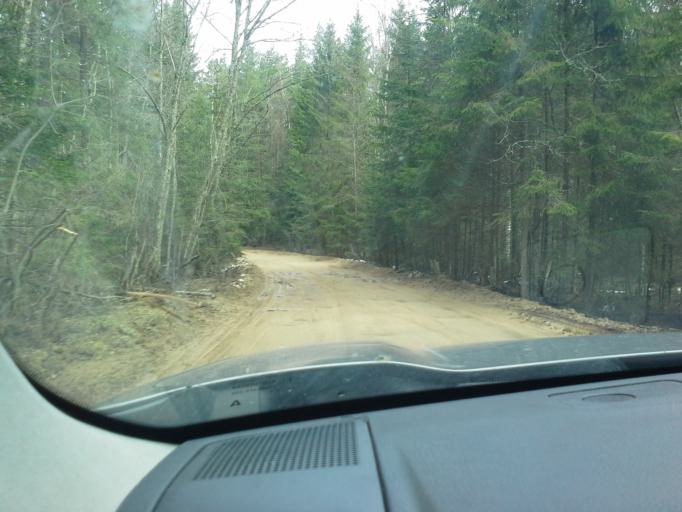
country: RU
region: Tverskaya
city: Ostashkov
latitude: 57.3435
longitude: 33.1087
